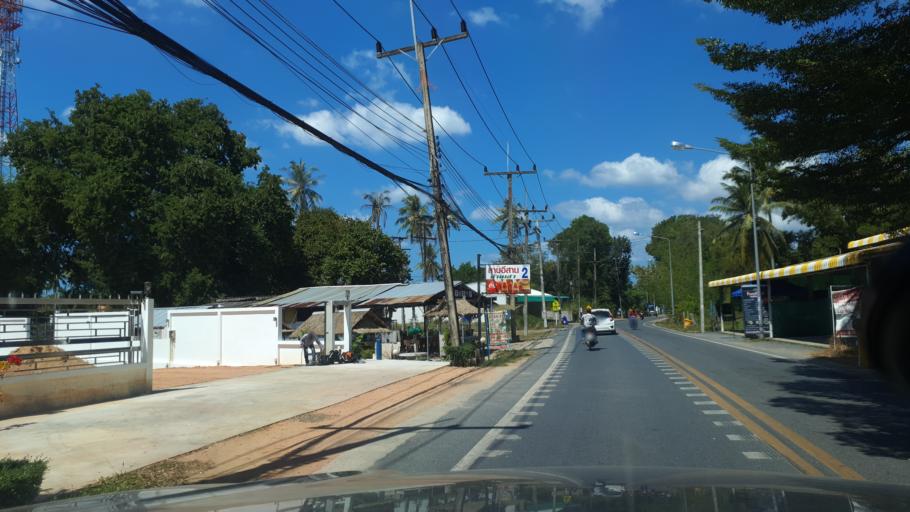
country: TH
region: Phuket
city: Thalang
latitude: 8.1300
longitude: 98.3080
